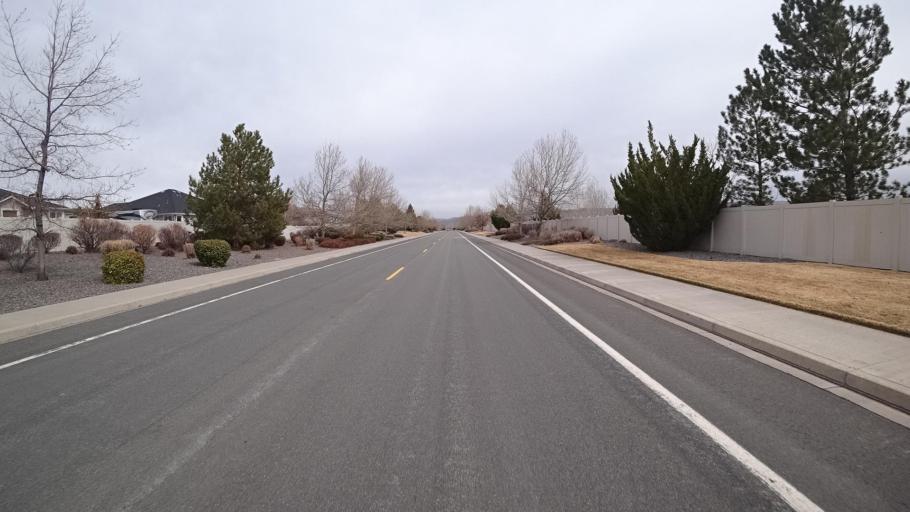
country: US
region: Nevada
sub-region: Washoe County
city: Spanish Springs
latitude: 39.6603
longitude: -119.7268
